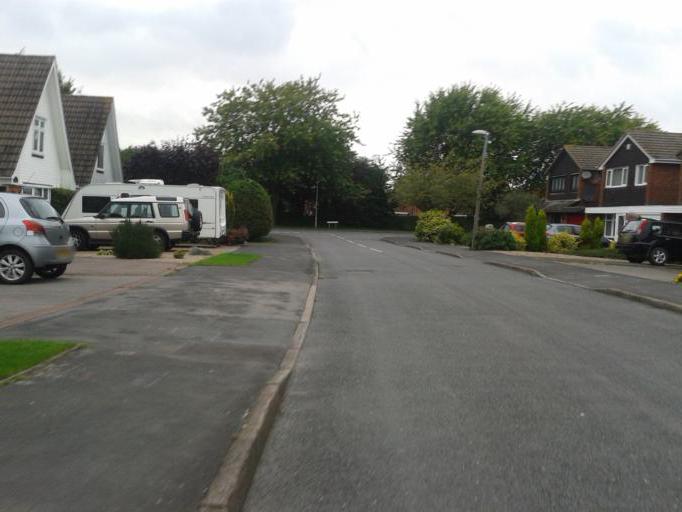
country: GB
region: England
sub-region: Leicestershire
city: Hinckley
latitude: 52.5550
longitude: -1.3578
